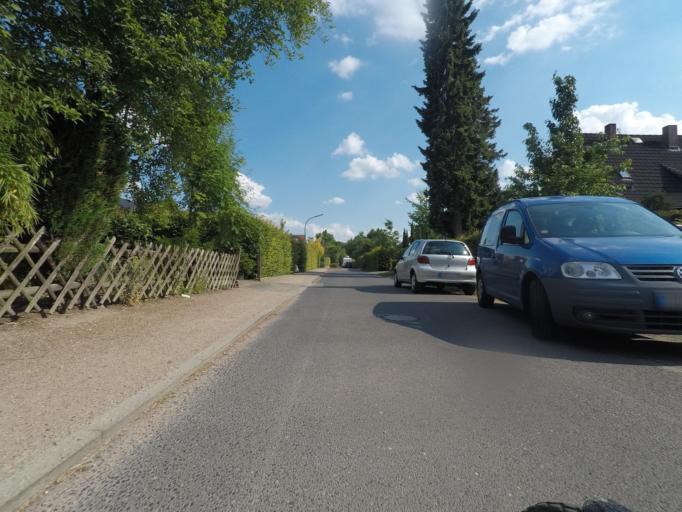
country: DE
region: Hamburg
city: Sasel
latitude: 53.6431
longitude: 10.1072
